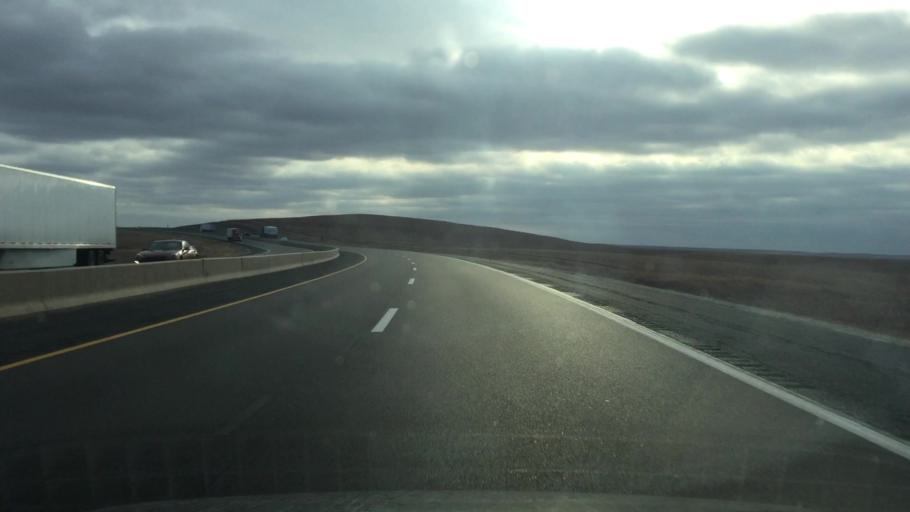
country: US
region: Kansas
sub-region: Chase County
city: Cottonwood Falls
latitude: 38.2195
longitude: -96.4330
